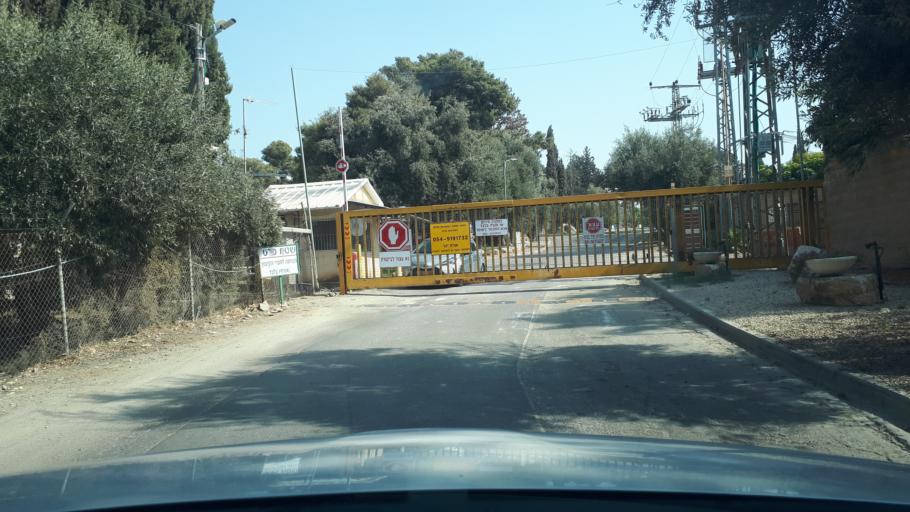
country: IL
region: Central District
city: Rosh Ha'Ayin
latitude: 32.0622
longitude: 34.9464
